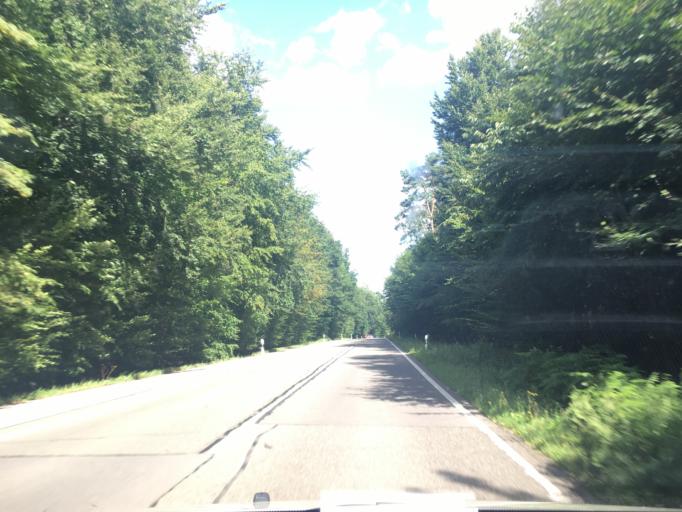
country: DE
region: Saarland
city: Sulzbach
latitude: 49.2755
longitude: 7.0810
